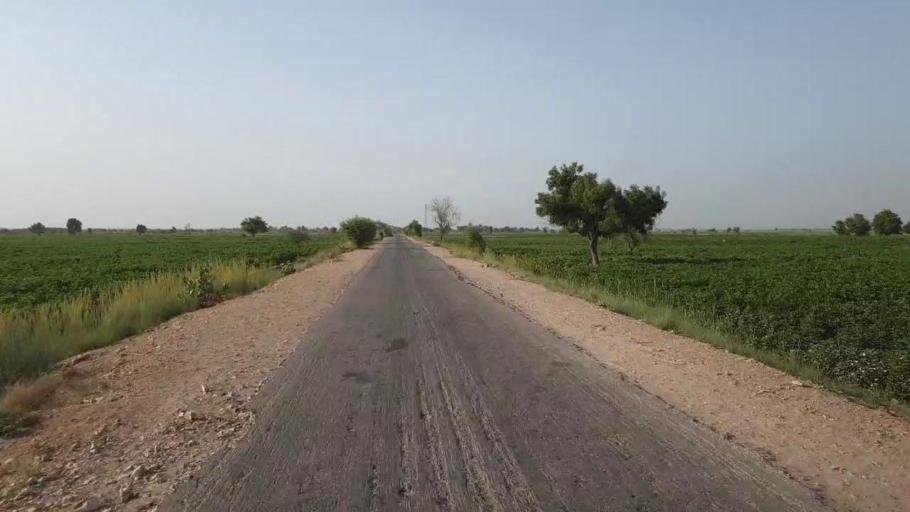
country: PK
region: Sindh
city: Jam Sahib
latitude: 26.4718
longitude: 68.8595
